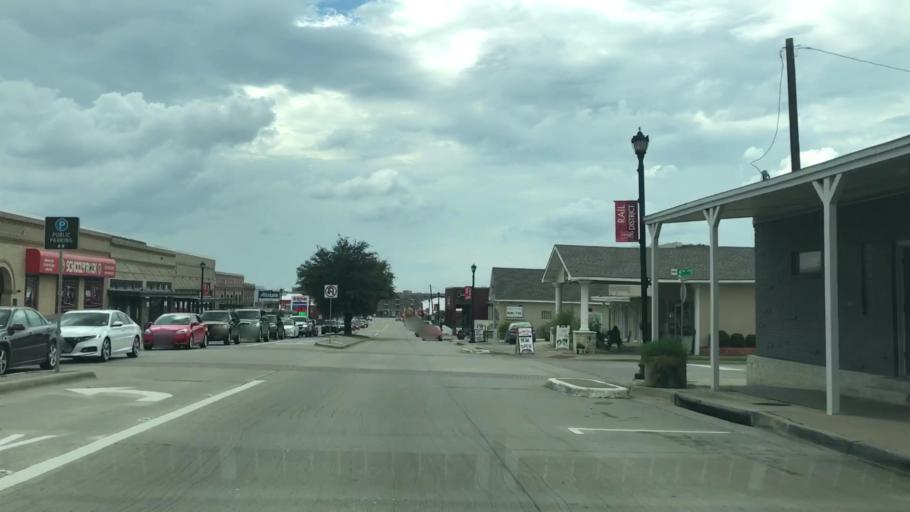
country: US
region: Texas
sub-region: Collin County
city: Frisco
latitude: 33.1507
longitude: -96.8248
